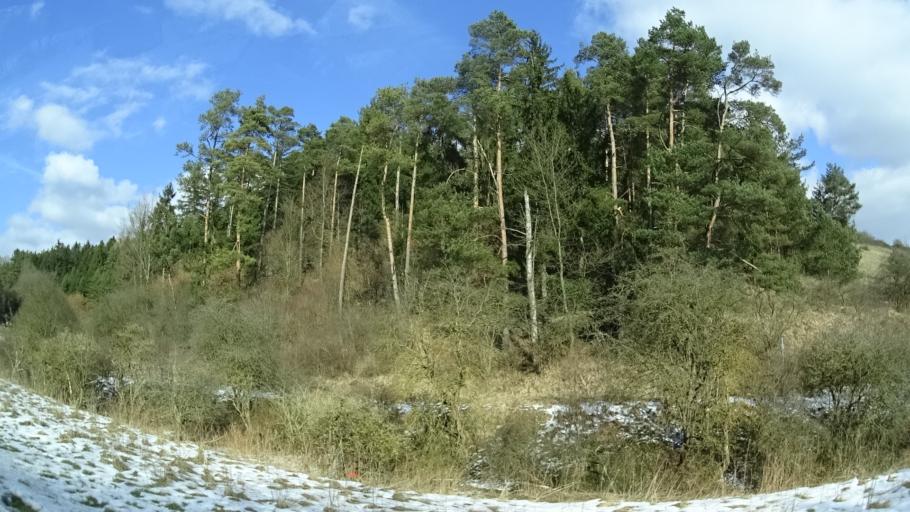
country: DE
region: Thuringia
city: Rohr
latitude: 50.5999
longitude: 10.5152
